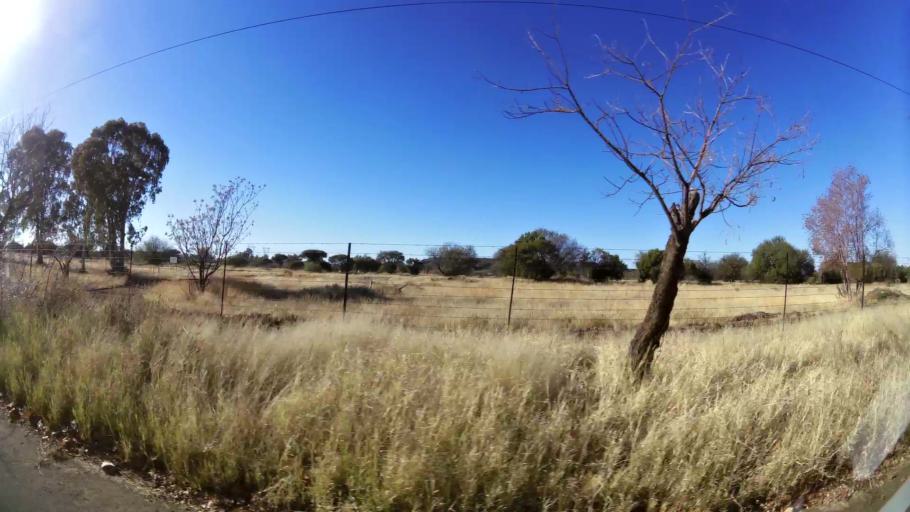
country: ZA
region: Northern Cape
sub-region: Frances Baard District Municipality
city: Kimberley
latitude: -28.7442
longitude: 24.7978
